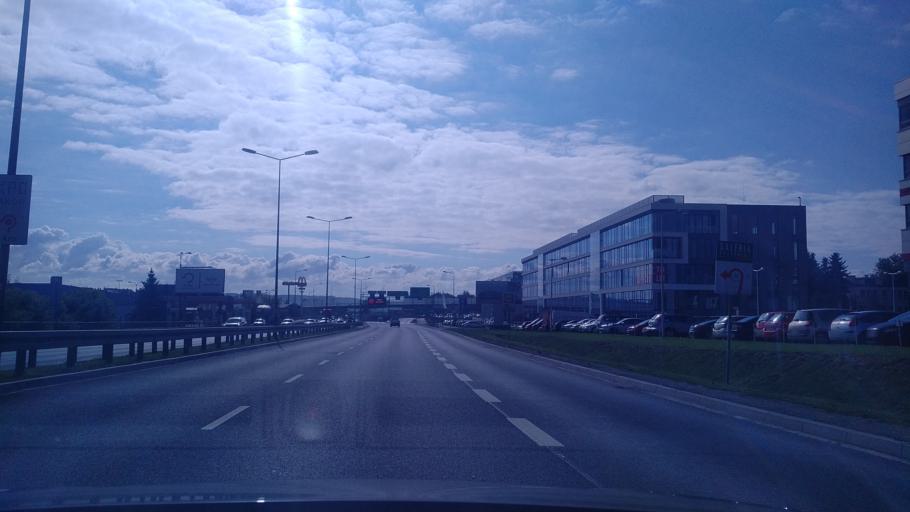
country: PL
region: Lesser Poland Voivodeship
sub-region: Powiat krakowski
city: Zielonki
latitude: 50.0913
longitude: 19.8931
